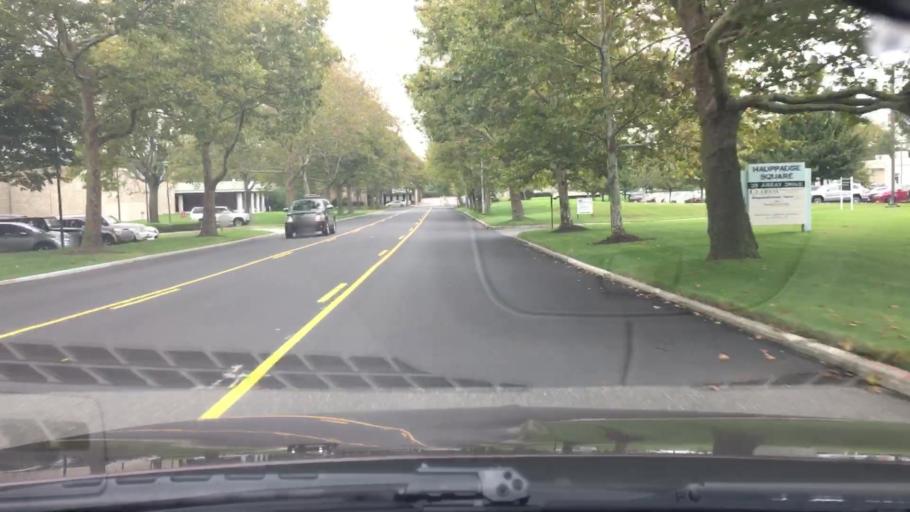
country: US
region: New York
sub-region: Suffolk County
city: Brentwood
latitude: 40.8125
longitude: -73.2494
